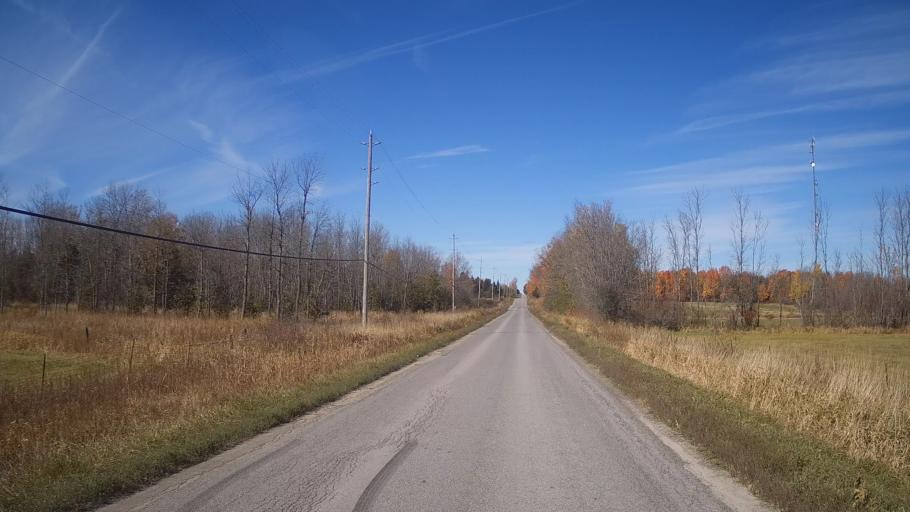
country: CA
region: Ontario
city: Perth
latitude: 44.8457
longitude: -76.3659
